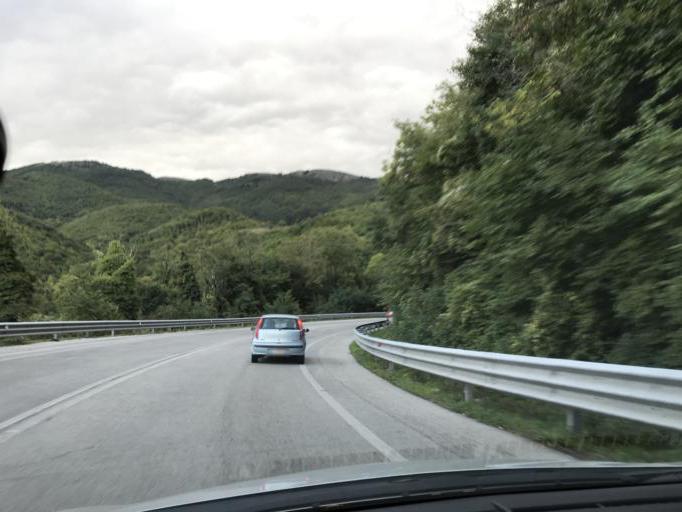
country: IT
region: Umbria
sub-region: Provincia di Terni
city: Ferentillo
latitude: 42.6680
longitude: 12.7312
